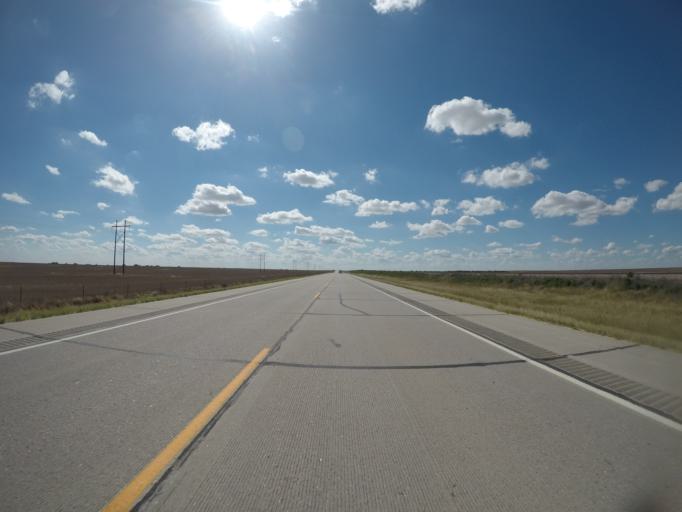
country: US
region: Colorado
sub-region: Phillips County
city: Holyoke
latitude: 40.5959
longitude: -102.3736
